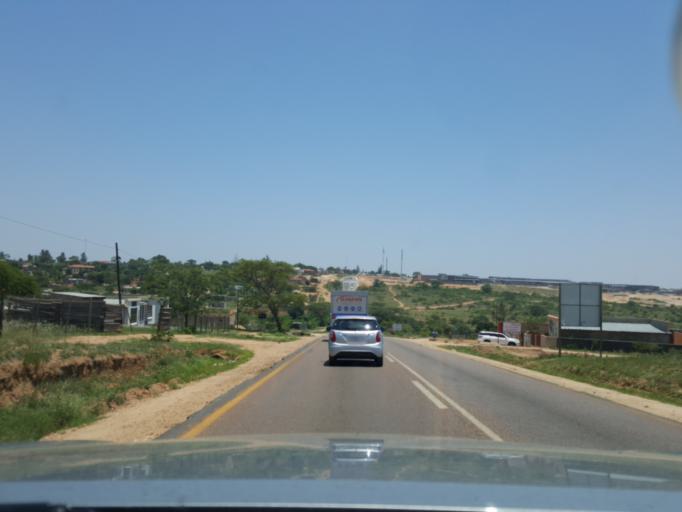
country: ZA
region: Limpopo
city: Thulamahashi
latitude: -24.6164
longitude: 31.0390
